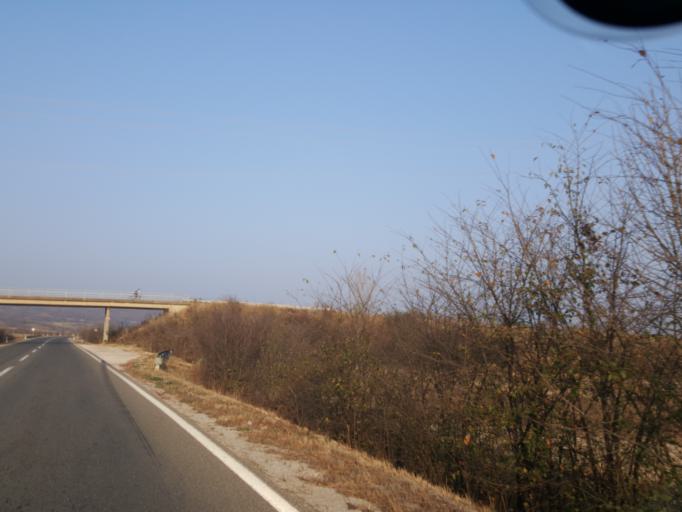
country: RS
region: Central Serbia
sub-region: Jablanicki Okrug
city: Leskovac
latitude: 42.9384
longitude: 22.0032
